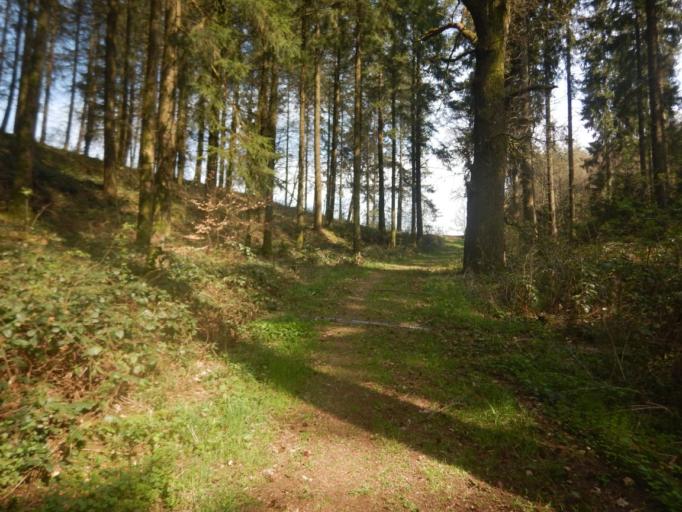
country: LU
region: Diekirch
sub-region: Canton de Clervaux
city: Clervaux
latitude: 50.0541
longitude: 6.0123
